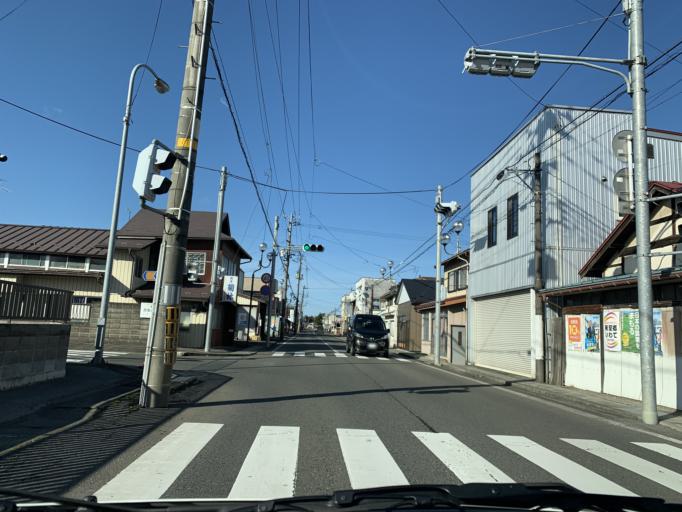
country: JP
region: Iwate
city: Mizusawa
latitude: 39.1971
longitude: 141.1182
